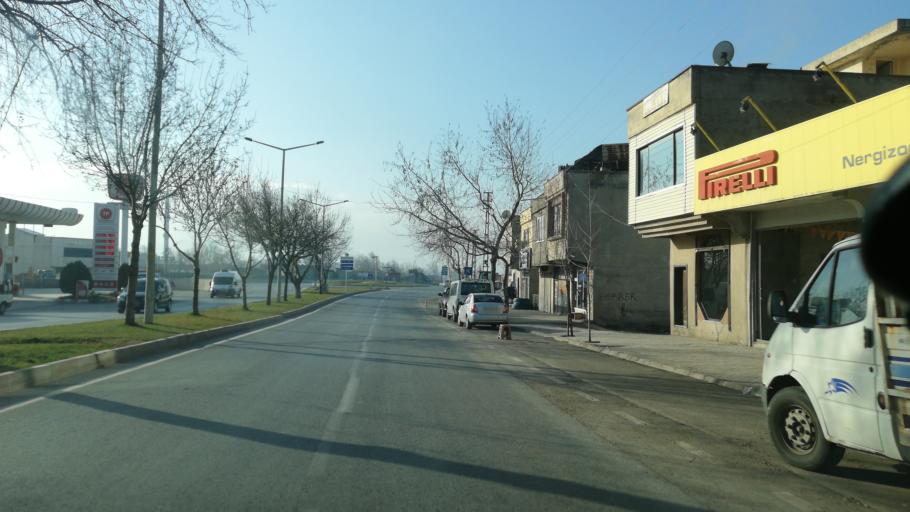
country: TR
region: Kahramanmaras
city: Kahramanmaras
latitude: 37.5633
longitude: 36.9172
